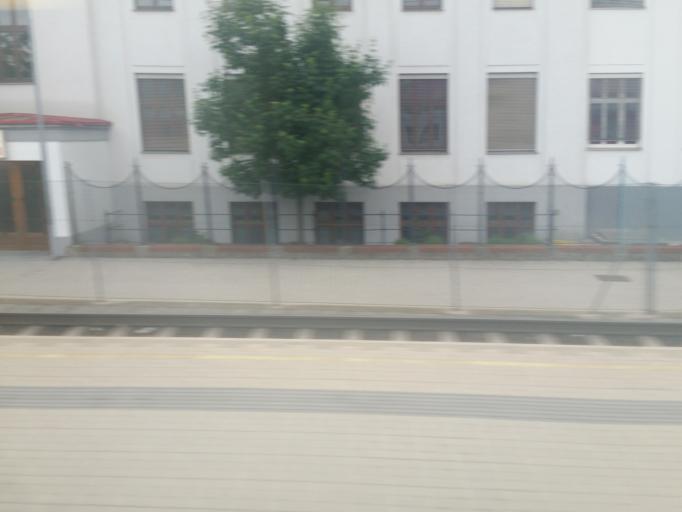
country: AT
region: Lower Austria
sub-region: Politischer Bezirk Wien-Umgebung
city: Gerasdorf bei Wien
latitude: 48.2305
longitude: 16.4542
